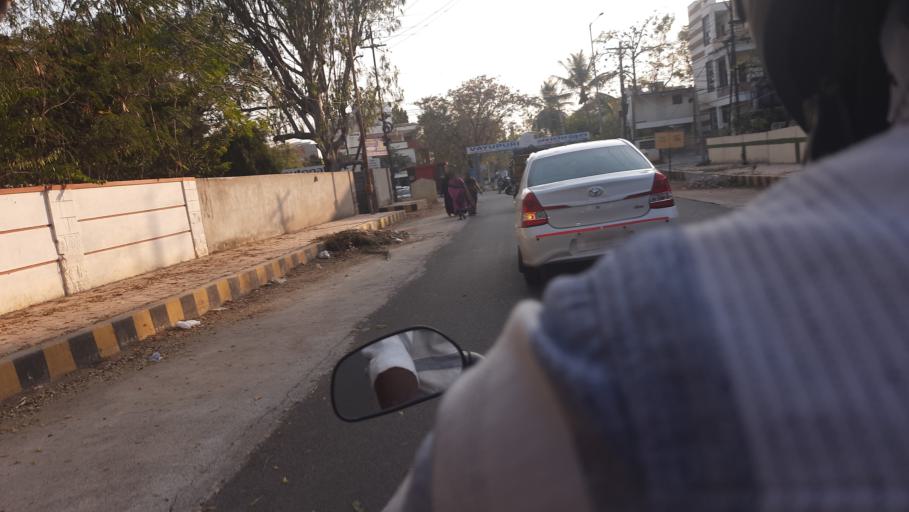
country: IN
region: Telangana
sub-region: Rangareddi
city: Secunderabad
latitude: 17.4856
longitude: 78.5473
